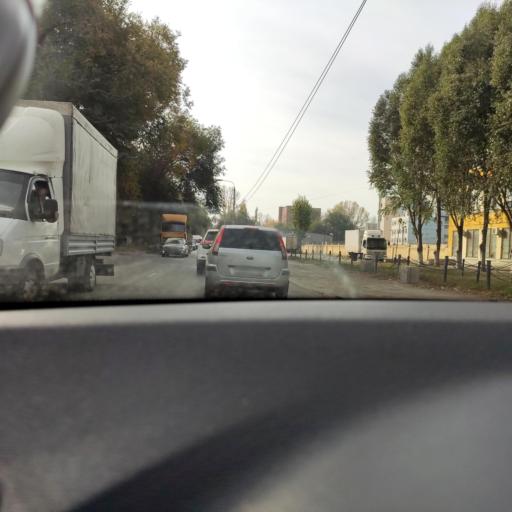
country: RU
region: Samara
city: Samara
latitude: 53.1925
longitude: 50.2454
